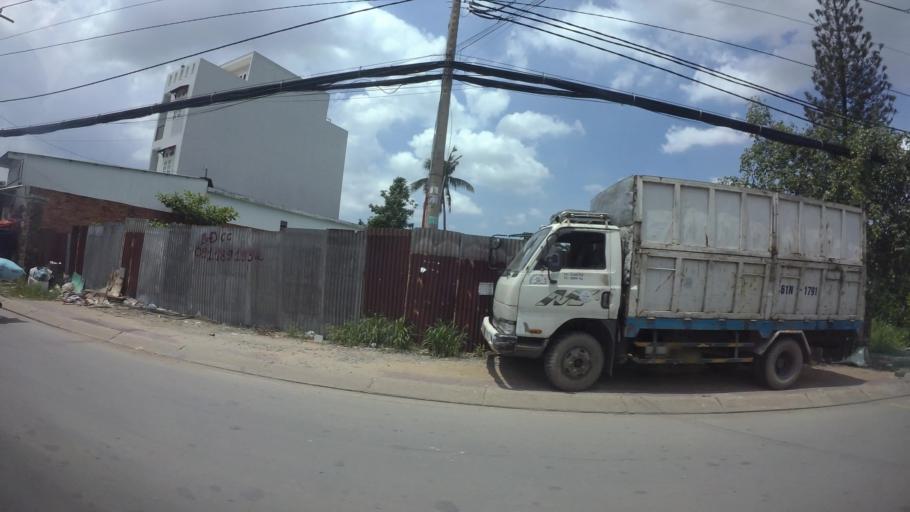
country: VN
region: Ho Chi Minh City
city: Quan Chin
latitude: 10.8360
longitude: 106.7823
